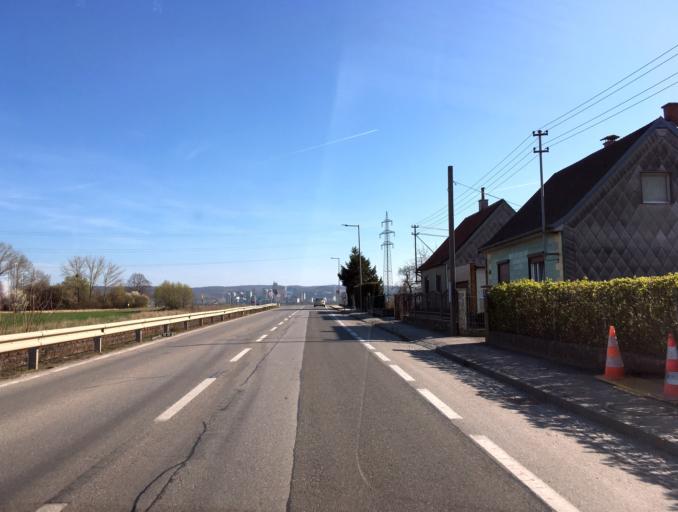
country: AT
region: Lower Austria
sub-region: Politischer Bezirk Bruck an der Leitha
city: Gotzendorf an der Leitha
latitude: 48.0078
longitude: 16.5866
